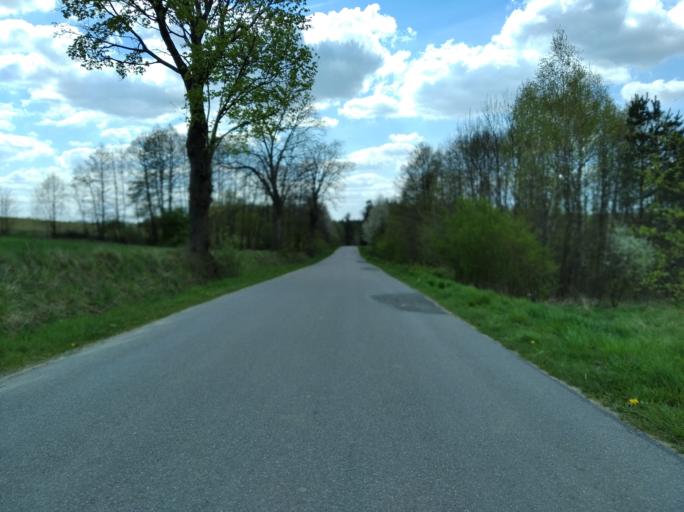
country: PL
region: Subcarpathian Voivodeship
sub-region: Powiat brzozowski
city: Wesola
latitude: 49.7647
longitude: 22.1271
